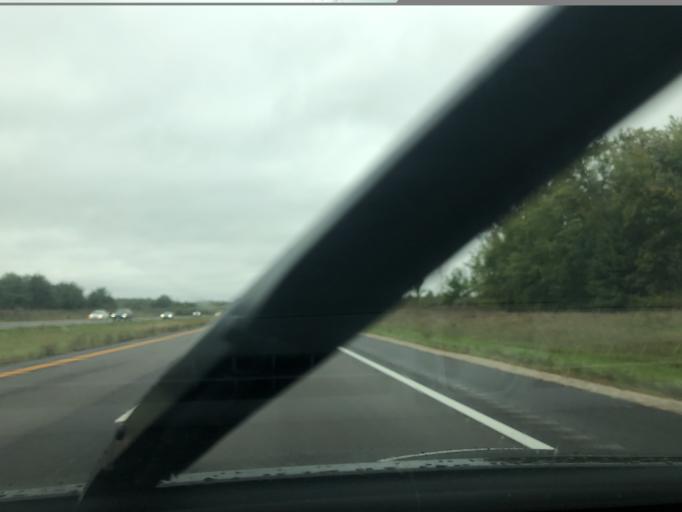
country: US
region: Ohio
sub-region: Union County
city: Marysville
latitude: 40.2552
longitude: -83.4501
